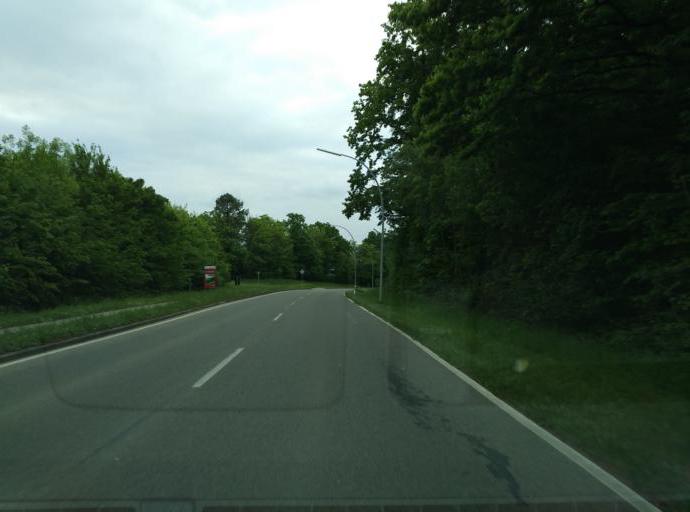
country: DE
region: Baden-Wuerttemberg
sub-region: Regierungsbezirk Stuttgart
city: Neuffen
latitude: 48.5614
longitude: 9.3815
